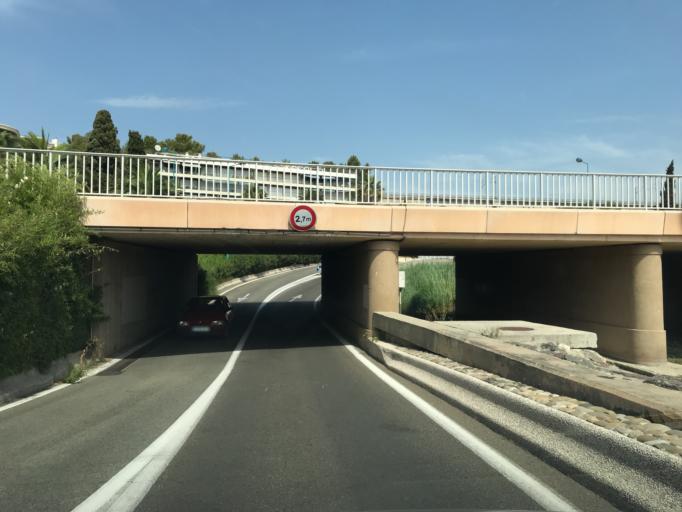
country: FR
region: Provence-Alpes-Cote d'Azur
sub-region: Departement du Var
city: Sanary-sur-Mer
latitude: 43.1391
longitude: 5.7697
